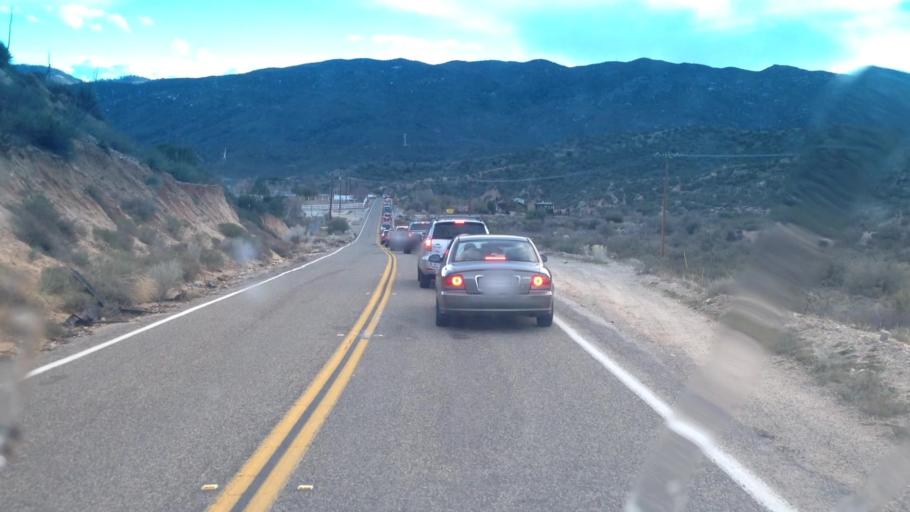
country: US
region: California
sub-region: San Bernardino County
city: Oak Hills
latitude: 34.3369
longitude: -117.3986
